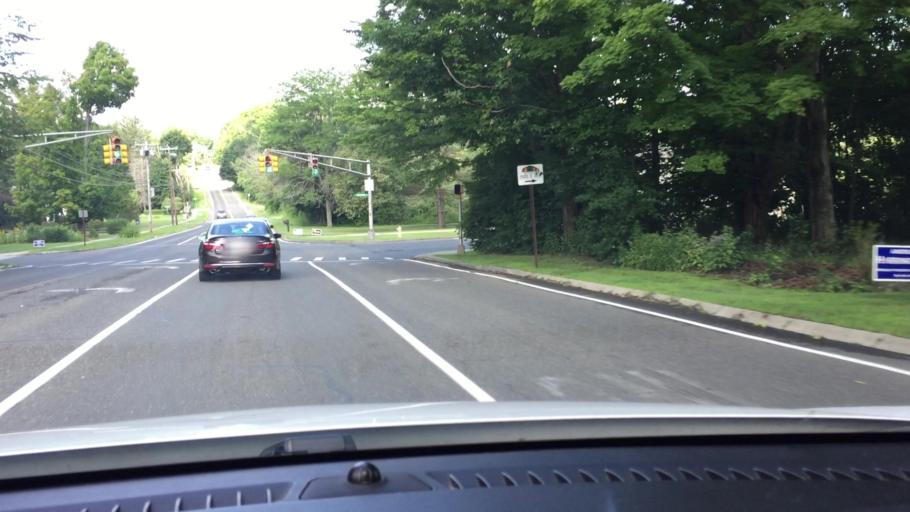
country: US
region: Massachusetts
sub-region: Berkshire County
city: Pittsfield
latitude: 42.4520
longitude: -73.2782
